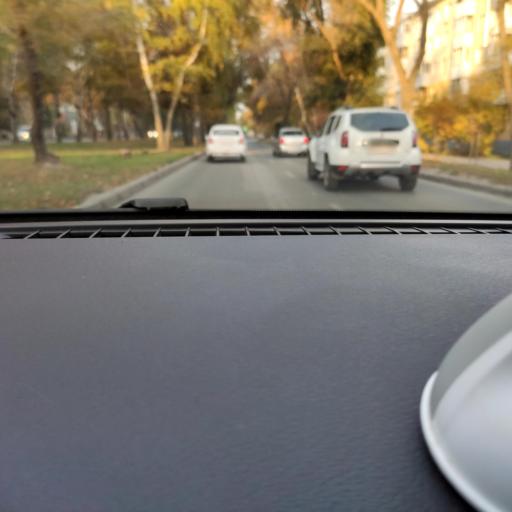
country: RU
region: Samara
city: Samara
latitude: 53.2143
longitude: 50.2325
